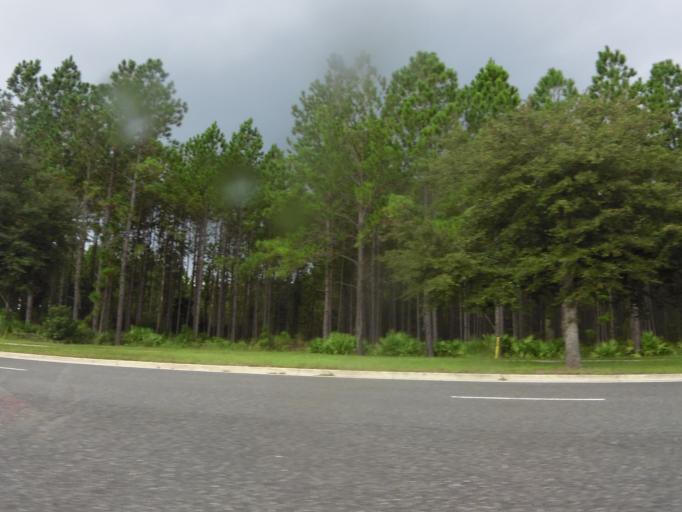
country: US
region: Florida
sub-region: Clay County
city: Lakeside
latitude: 30.1915
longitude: -81.8471
